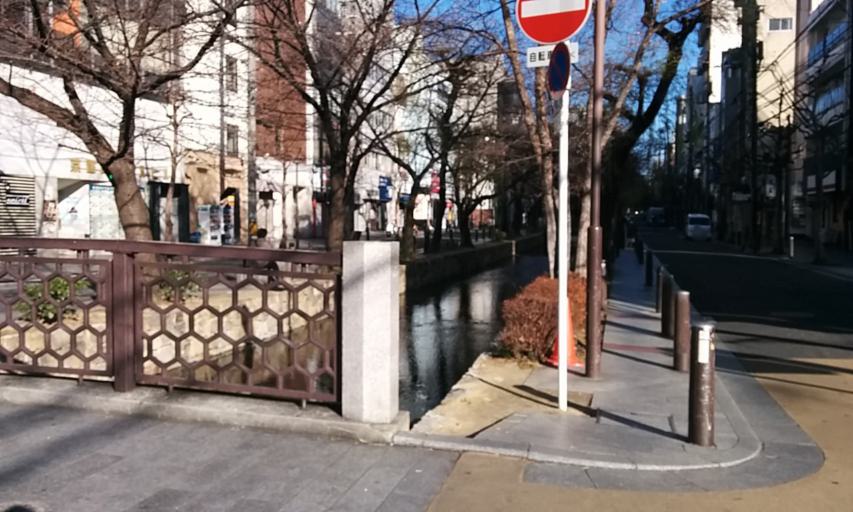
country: JP
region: Kyoto
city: Kyoto
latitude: 35.0066
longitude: 135.7705
